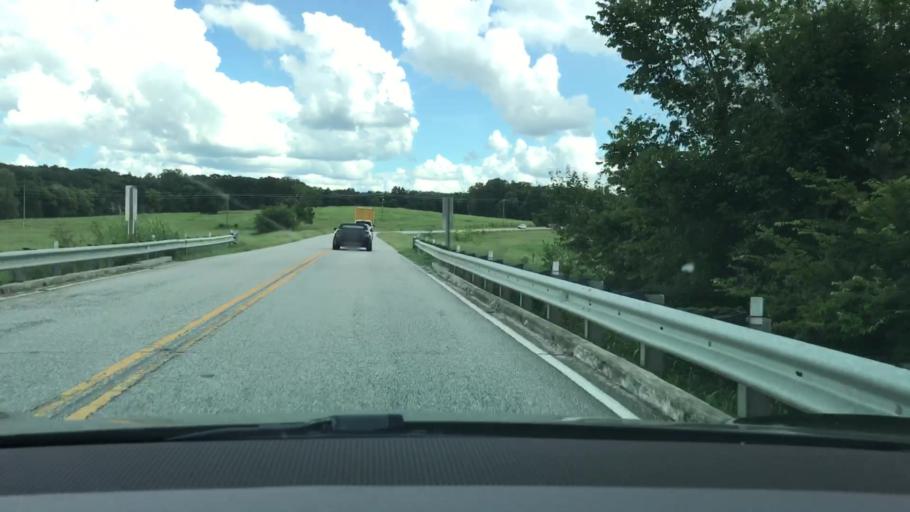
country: US
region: Alabama
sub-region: Montgomery County
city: Pike Road
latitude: 32.2558
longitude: -86.0963
